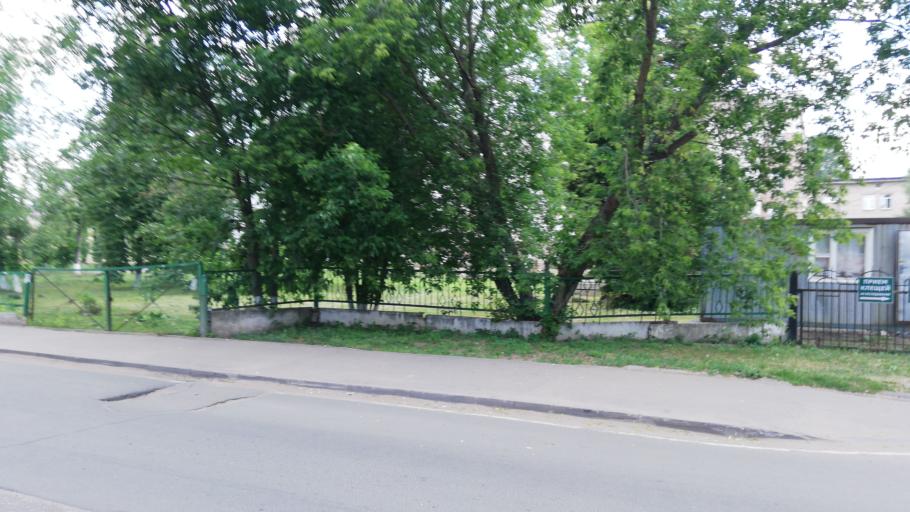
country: RU
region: Jaroslavl
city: Yaroslavl
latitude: 57.6381
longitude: 39.8631
